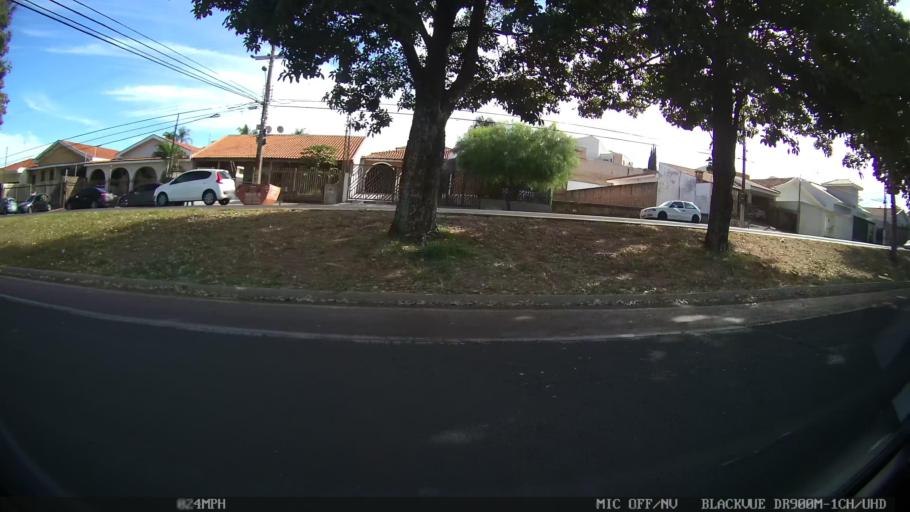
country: BR
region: Sao Paulo
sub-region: Catanduva
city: Catanduva
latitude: -21.1194
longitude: -48.9712
